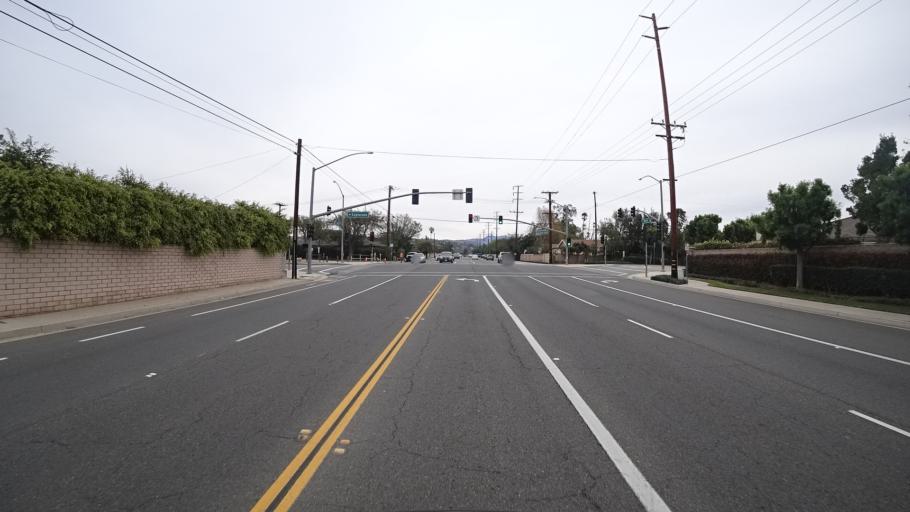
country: US
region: California
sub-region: Orange County
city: North Tustin
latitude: 33.7599
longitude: -117.8123
